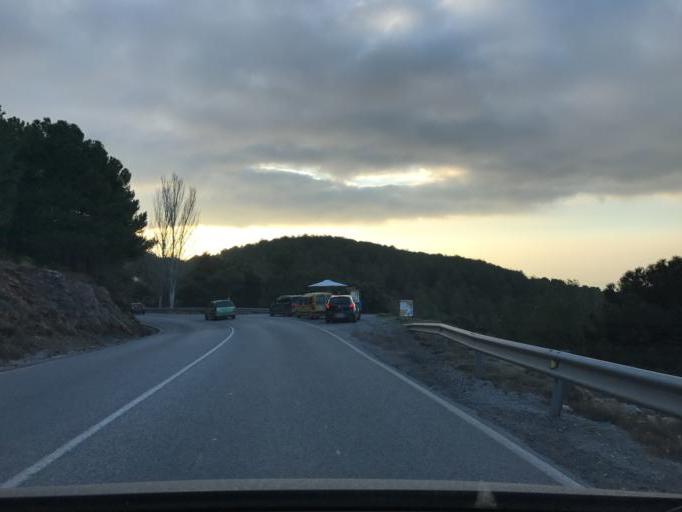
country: ES
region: Andalusia
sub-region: Provincia de Granada
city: Guejar-Sierra
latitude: 37.1389
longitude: -3.4580
